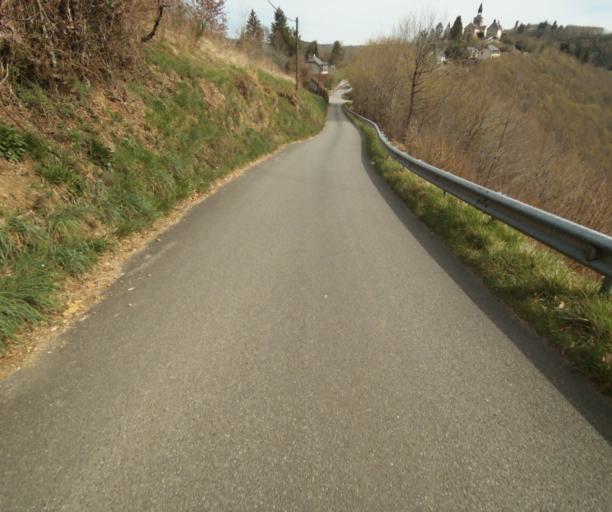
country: FR
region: Limousin
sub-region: Departement de la Correze
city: Naves
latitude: 45.3434
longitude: 1.8118
